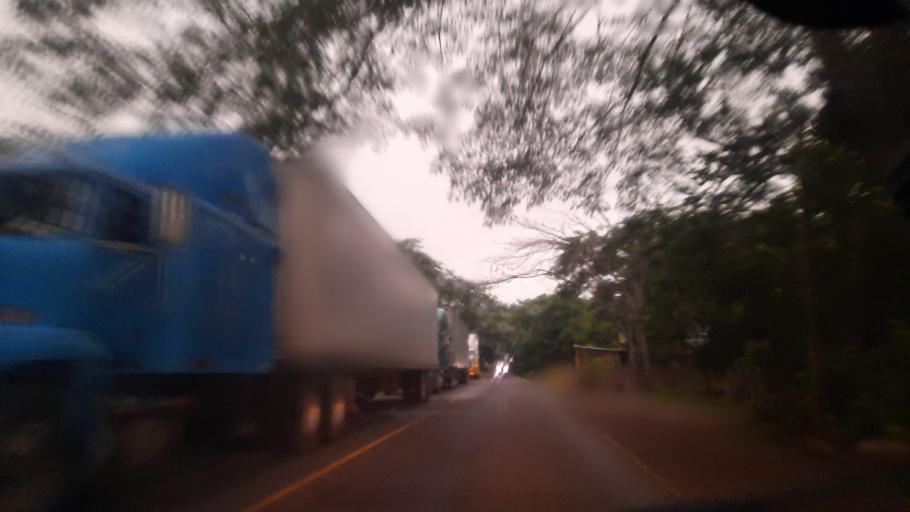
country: GT
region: Jutiapa
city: Atescatempa
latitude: 14.1995
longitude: -89.6790
